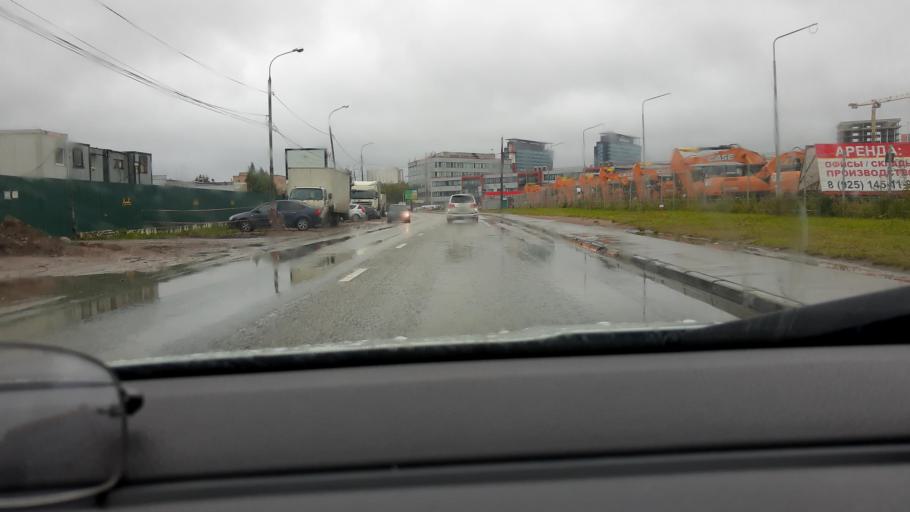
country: RU
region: Moscow
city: Khimki
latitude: 55.9143
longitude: 37.4203
